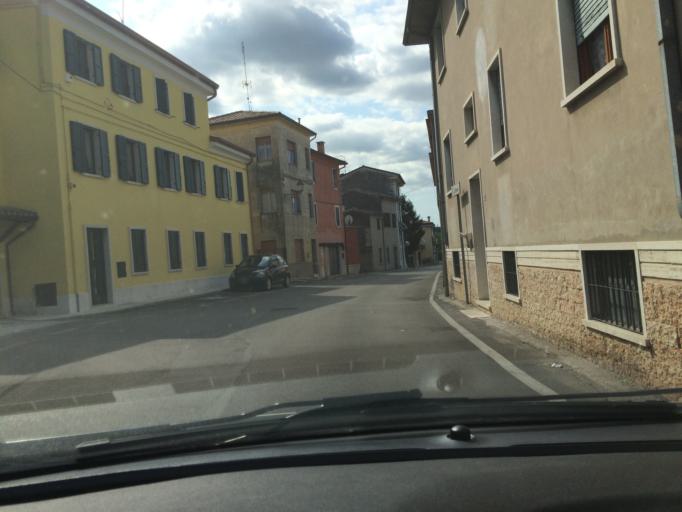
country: IT
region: Veneto
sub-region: Provincia di Verona
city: Volargne
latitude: 45.5205
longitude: 10.8063
